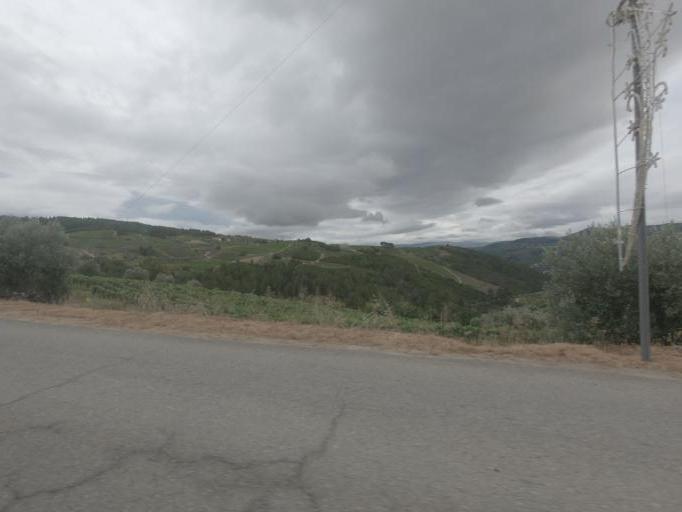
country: PT
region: Vila Real
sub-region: Sabrosa
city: Sabrosa
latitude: 41.2828
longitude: -7.5326
